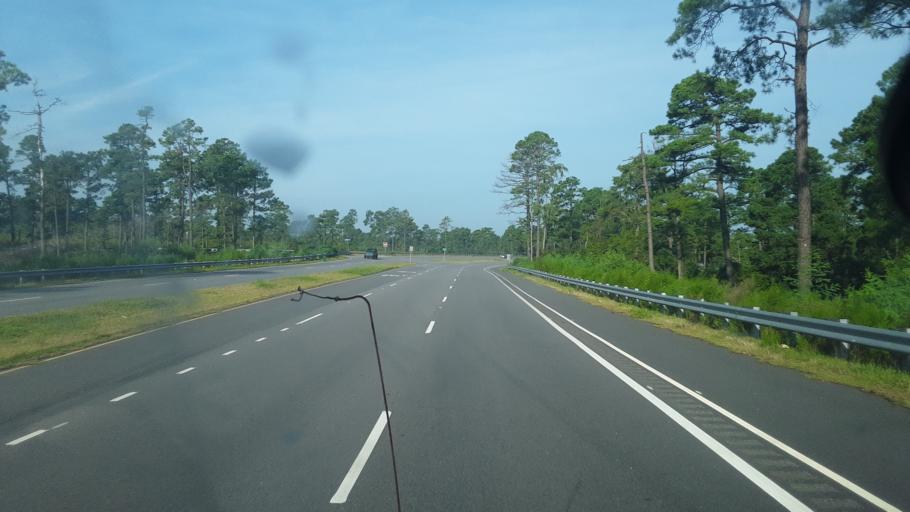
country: US
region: South Carolina
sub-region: Horry County
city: Forestbrook
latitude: 33.8177
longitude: -78.9079
